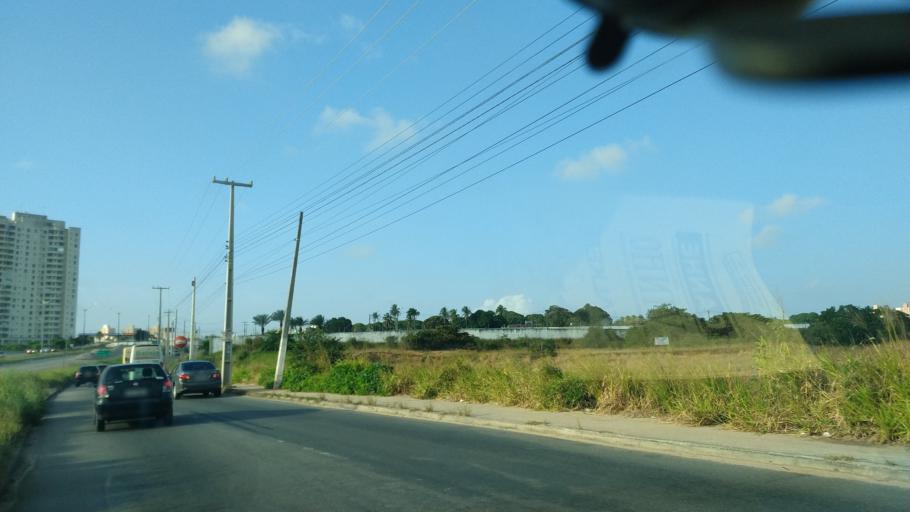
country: BR
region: Rio Grande do Norte
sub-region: Parnamirim
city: Parnamirim
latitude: -5.8807
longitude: -35.2252
